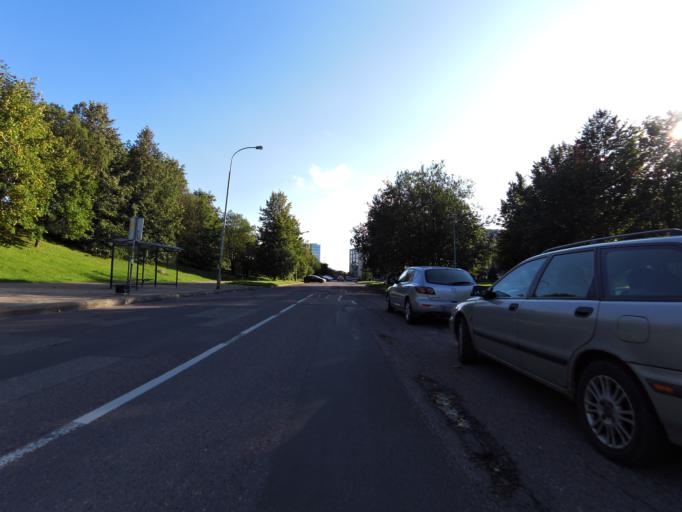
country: LT
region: Vilnius County
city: Justiniskes
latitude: 54.7096
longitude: 25.2133
